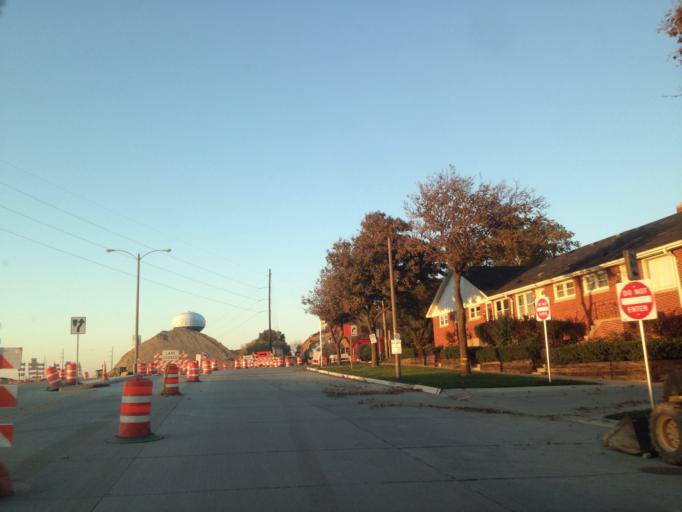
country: US
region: Wisconsin
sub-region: Milwaukee County
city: Wauwatosa
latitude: 43.0377
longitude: -88.0315
